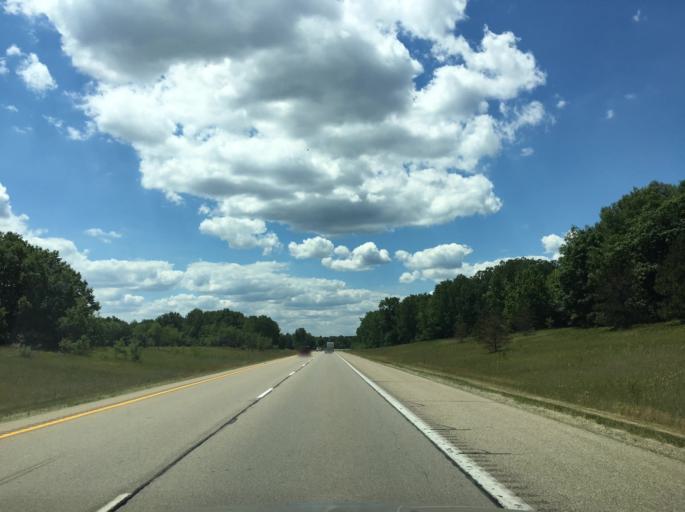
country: US
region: Michigan
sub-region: Clare County
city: Clare
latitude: 43.8800
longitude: -84.8153
